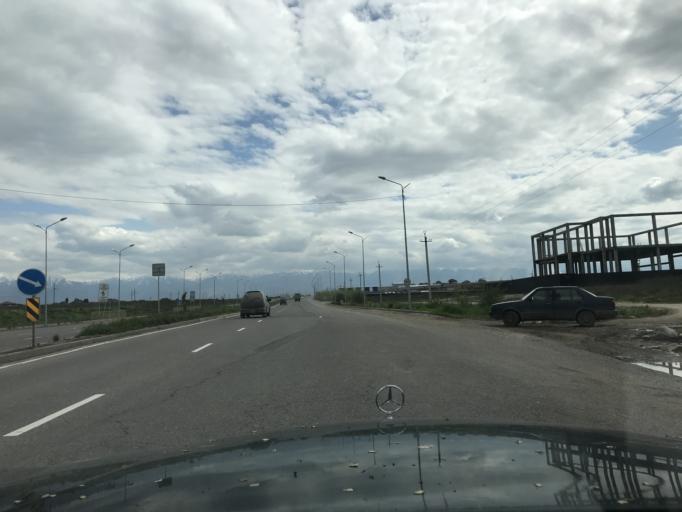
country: KZ
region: Almaty Oblysy
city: Burunday
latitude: 43.3481
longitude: 76.8337
